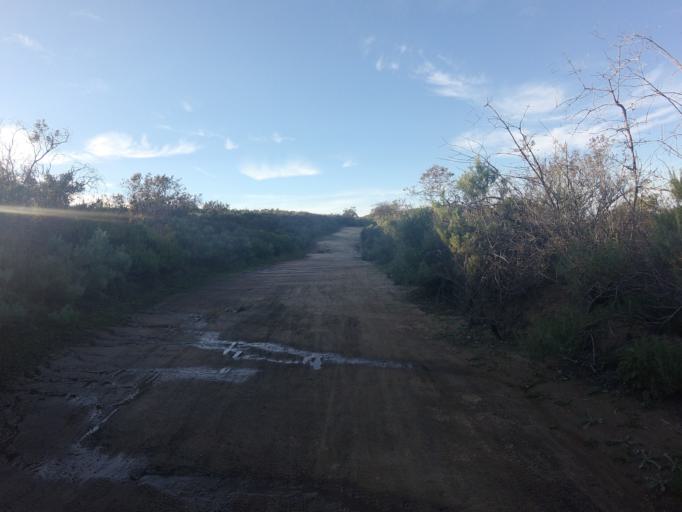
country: US
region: California
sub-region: Orange County
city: Laguna Beach
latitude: 33.5905
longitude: -117.7769
